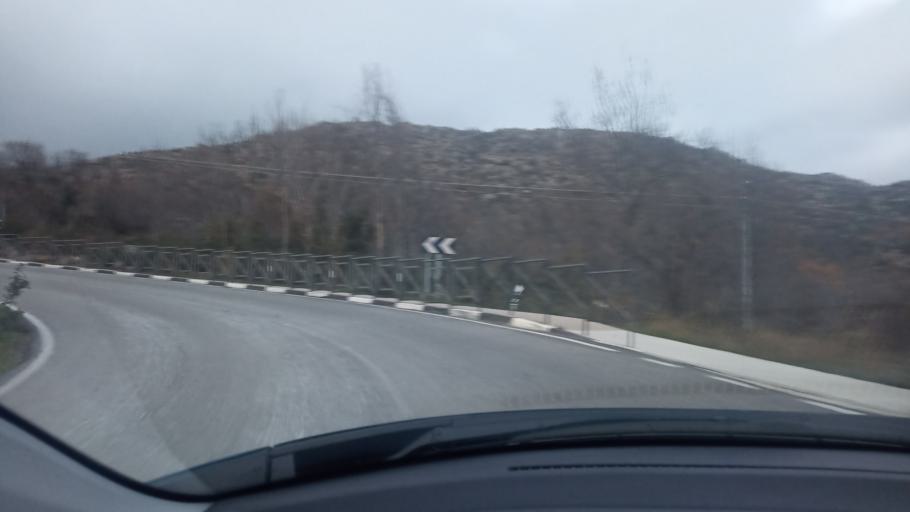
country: ES
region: Madrid
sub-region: Provincia de Madrid
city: Zarzalejo
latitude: 40.5469
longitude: -4.1734
